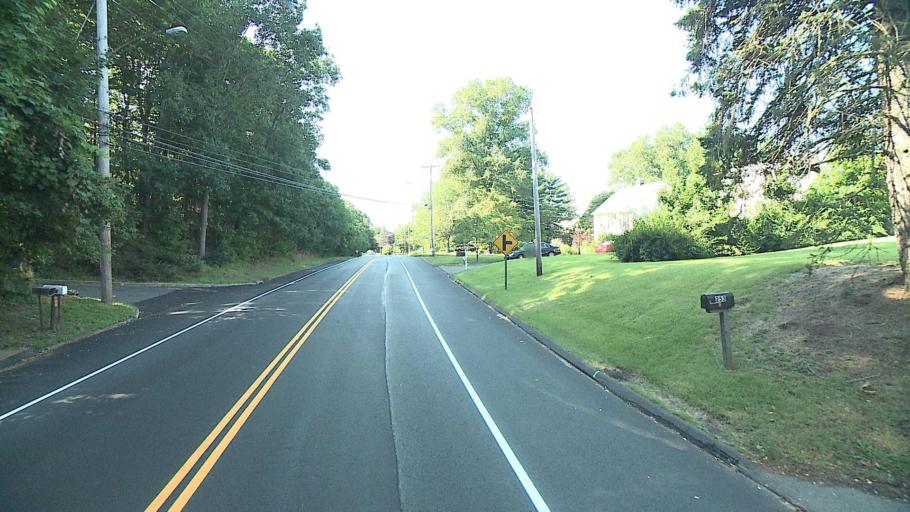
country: US
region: Connecticut
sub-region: Fairfield County
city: Trumbull
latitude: 41.2305
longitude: -73.1773
